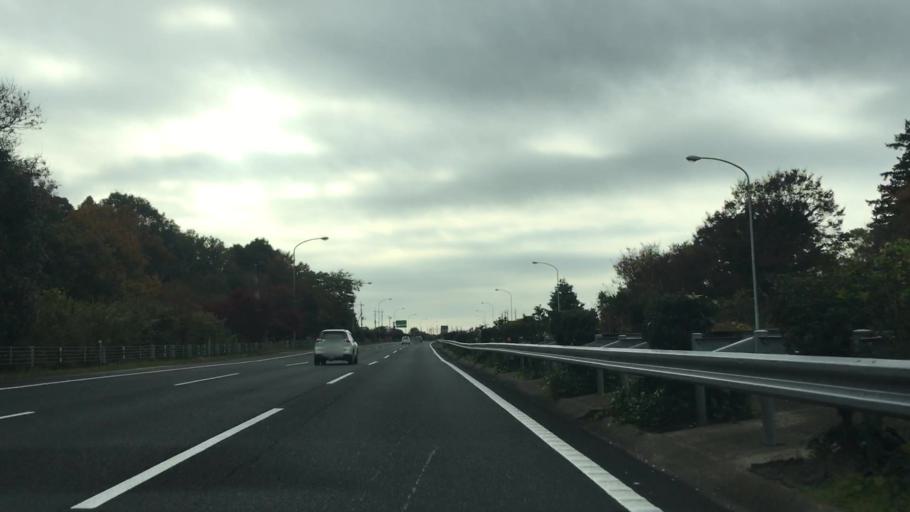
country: JP
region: Chiba
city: Narita
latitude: 35.7551
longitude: 140.3192
